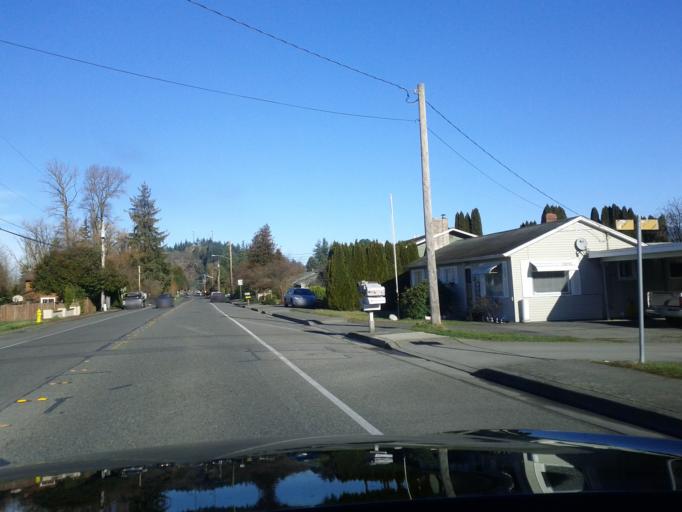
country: US
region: Washington
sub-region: Skagit County
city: Burlington
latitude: 48.4659
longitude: -122.3248
